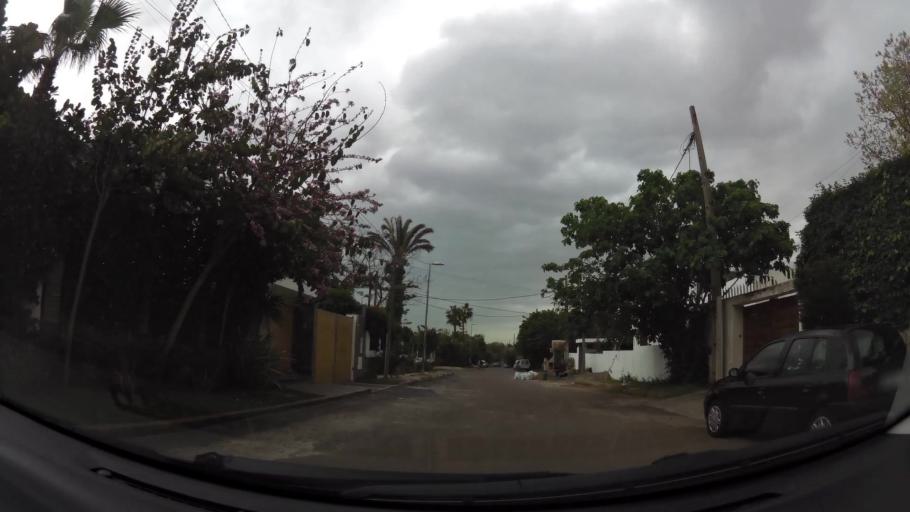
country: MA
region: Grand Casablanca
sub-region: Casablanca
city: Casablanca
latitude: 33.5779
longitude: -7.6634
